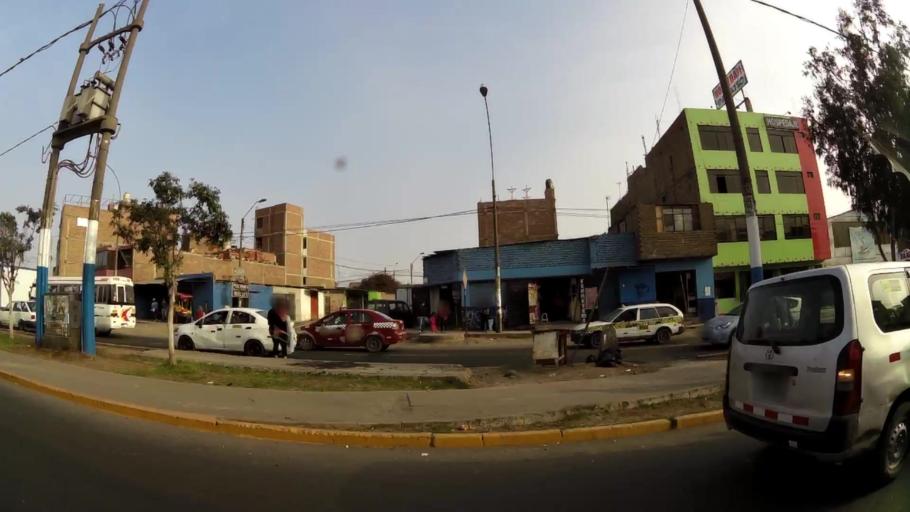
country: PE
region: Lima
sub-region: Lima
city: Independencia
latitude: -12.0262
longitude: -77.0770
